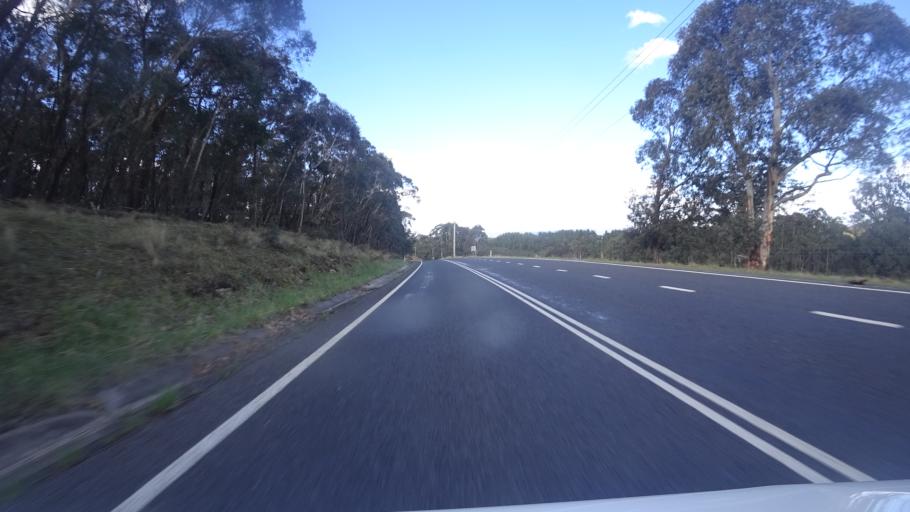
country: AU
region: New South Wales
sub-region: Lithgow
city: Bowenfels
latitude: -33.6341
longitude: 150.0835
